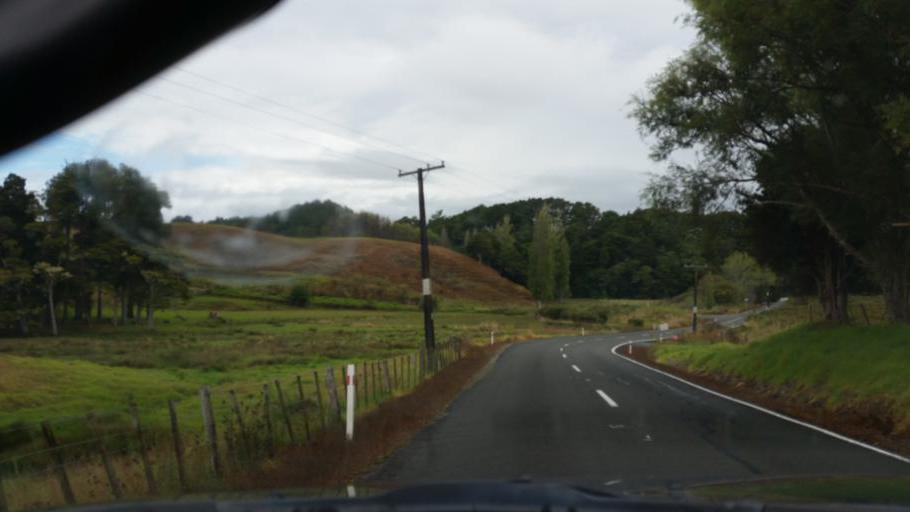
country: NZ
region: Auckland
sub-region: Auckland
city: Wellsford
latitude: -36.1234
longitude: 174.3610
